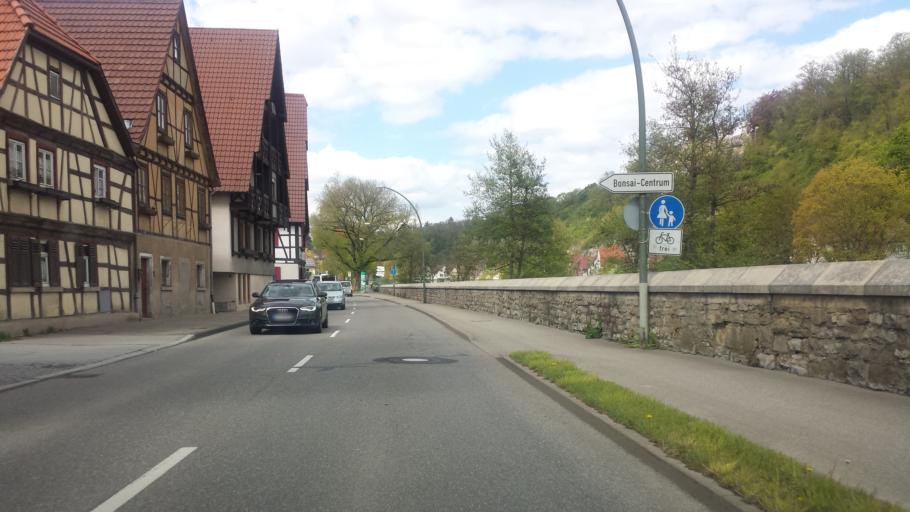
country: DE
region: Baden-Wuerttemberg
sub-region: Karlsruhe Region
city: Muhlacker
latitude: 48.9389
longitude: 8.8422
